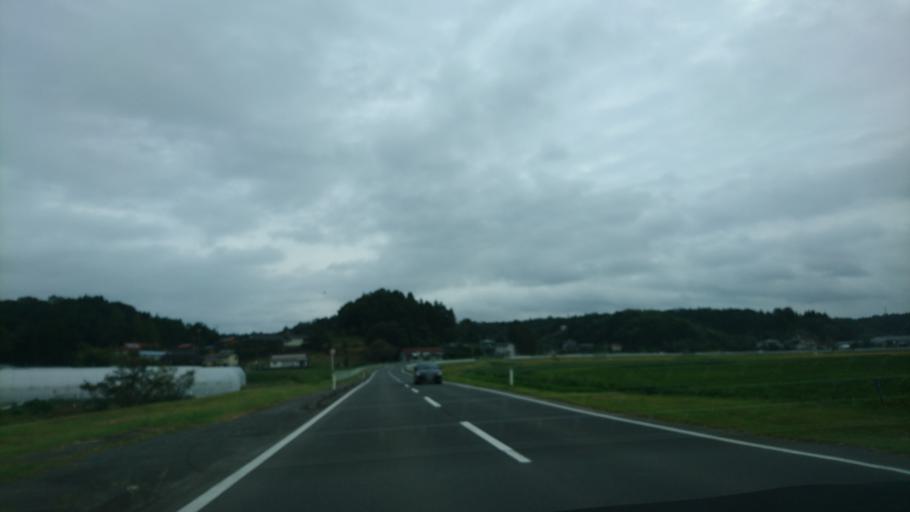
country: JP
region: Iwate
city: Ichinoseki
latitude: 38.8045
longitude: 141.1068
